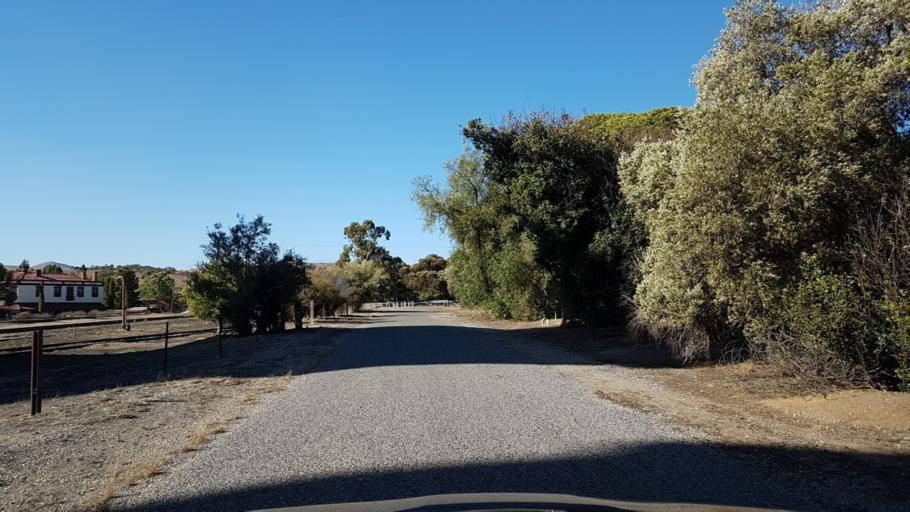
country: AU
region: South Australia
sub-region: Clare and Gilbert Valleys
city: Clare
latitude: -33.6728
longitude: 138.9216
